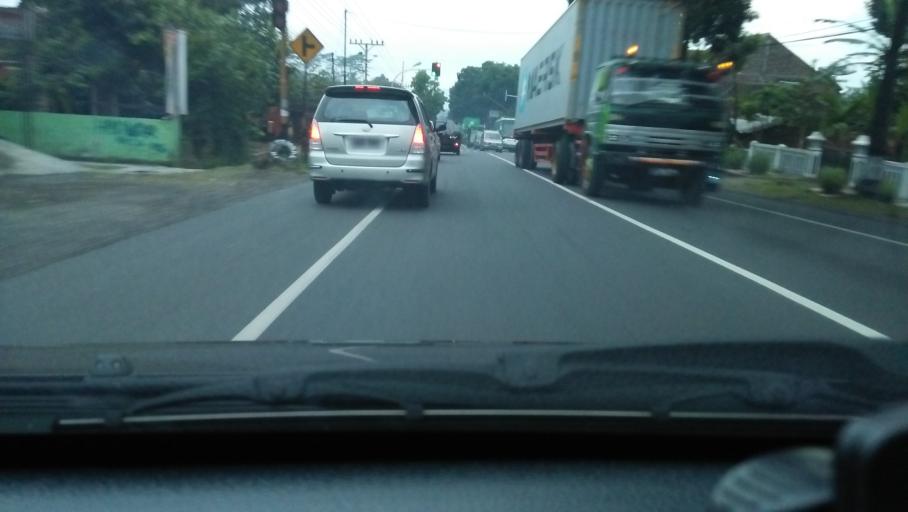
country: ID
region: Central Java
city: Magelang
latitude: -7.4056
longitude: 110.2392
